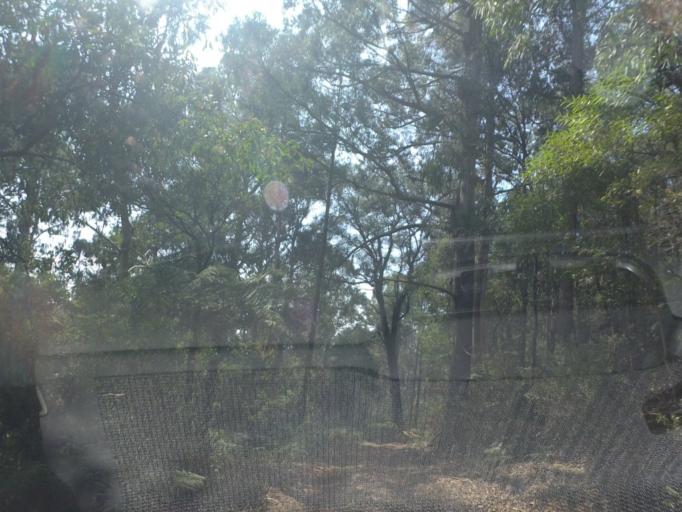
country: AU
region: Victoria
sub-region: Yarra Ranges
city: Healesville
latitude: -37.5640
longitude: 145.6206
